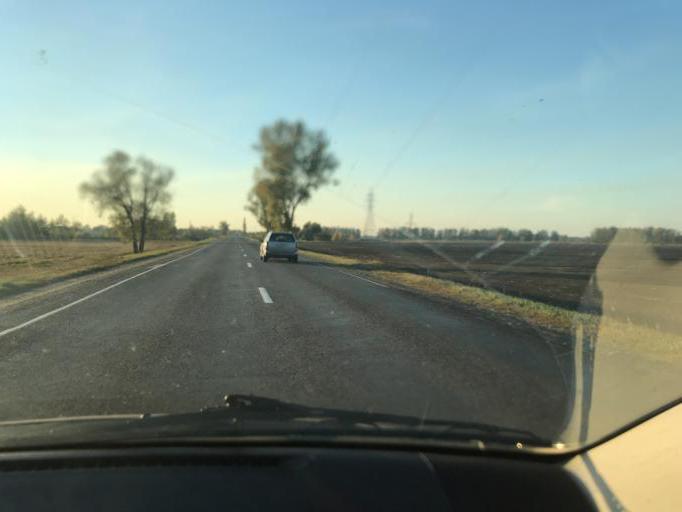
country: BY
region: Brest
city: Pinsk
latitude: 52.0688
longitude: 26.1829
